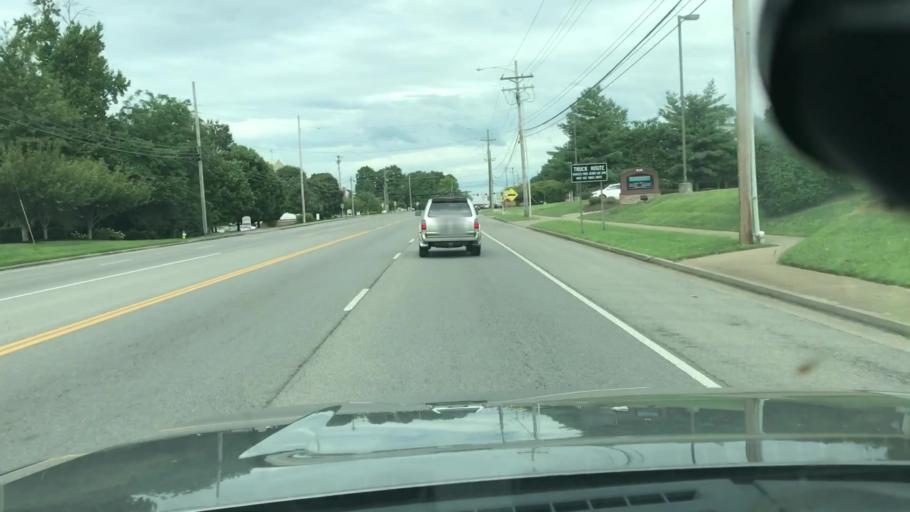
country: US
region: Tennessee
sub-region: Williamson County
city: Franklin
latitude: 35.9167
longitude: -86.8406
